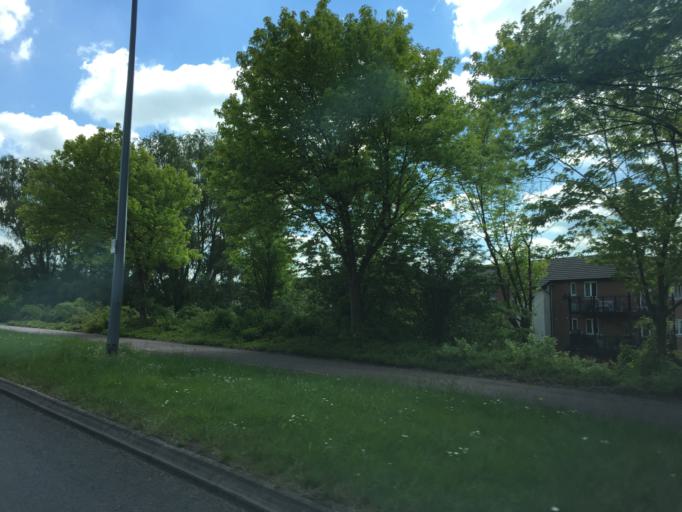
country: GB
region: England
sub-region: Milton Keynes
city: Milton Keynes
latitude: 52.0352
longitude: -0.7528
